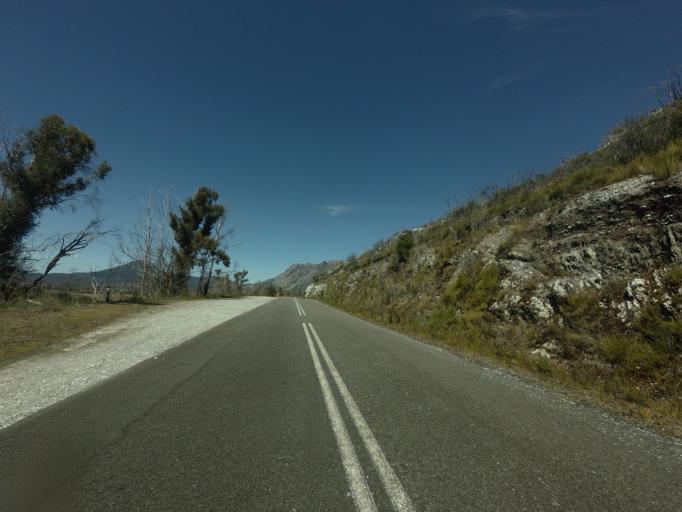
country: AU
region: Tasmania
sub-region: Huon Valley
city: Geeveston
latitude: -42.8515
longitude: 146.1828
